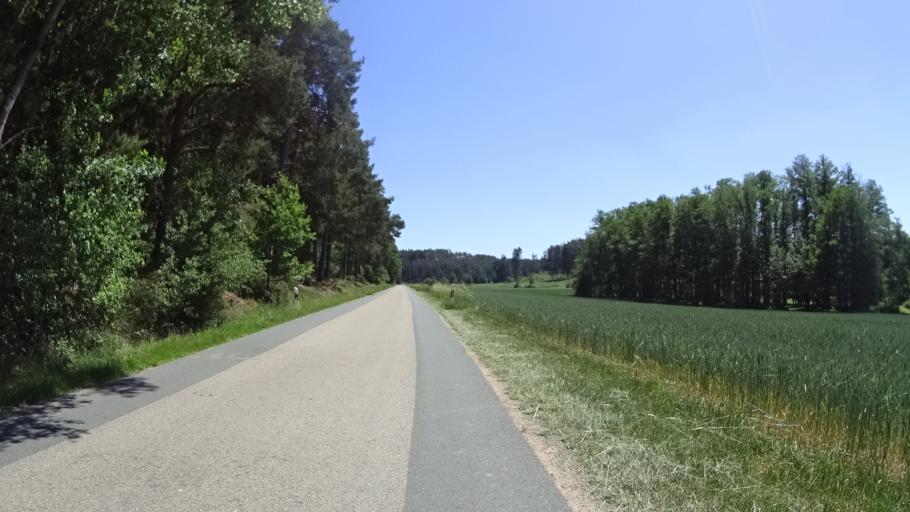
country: DE
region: Bavaria
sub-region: Regierungsbezirk Mittelfranken
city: Pleinfeld
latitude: 49.0828
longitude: 10.9803
